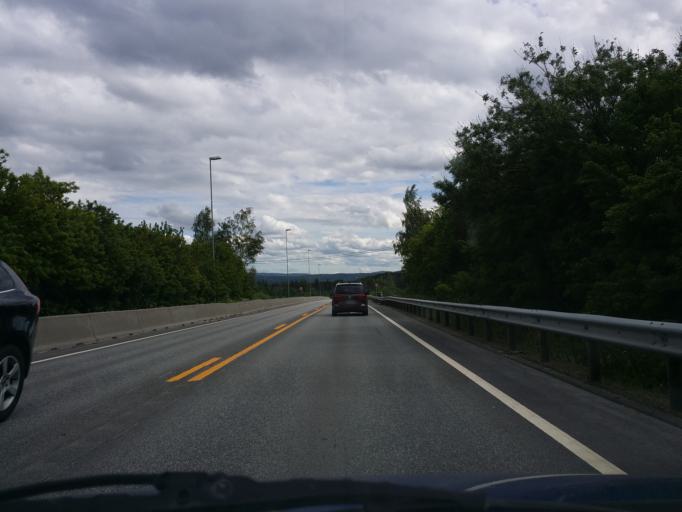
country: NO
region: Hedmark
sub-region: Stange
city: Stange
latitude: 60.7266
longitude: 11.2245
